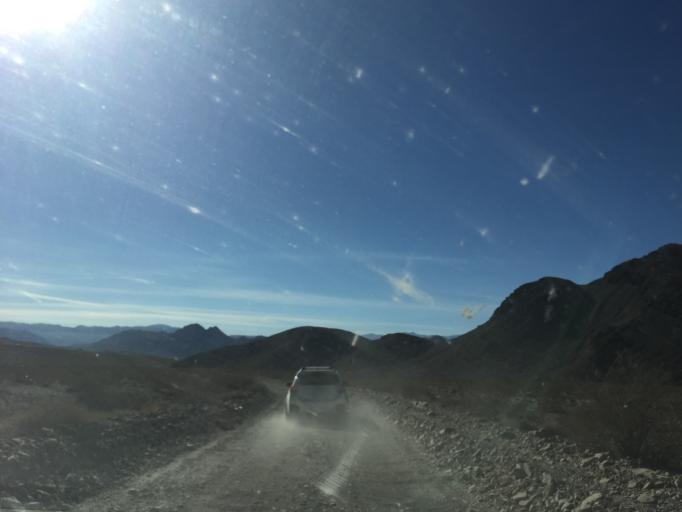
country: US
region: California
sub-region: Inyo County
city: Lone Pine
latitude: 36.7703
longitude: -117.5336
